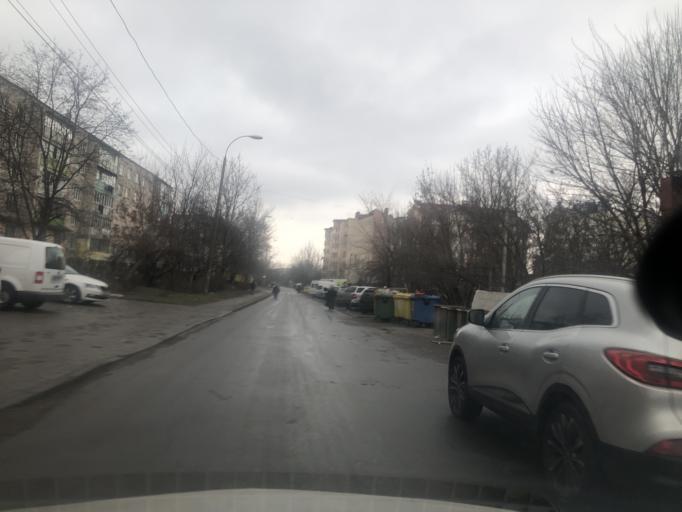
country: MD
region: Chisinau
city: Stauceni
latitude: 47.0620
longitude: 28.8437
